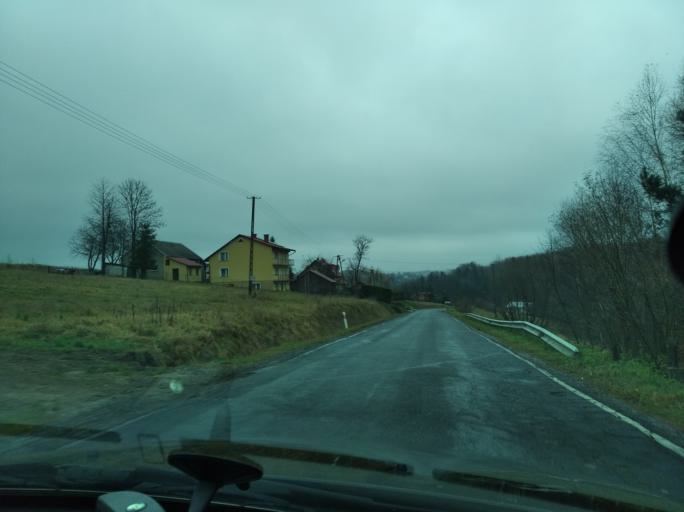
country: PL
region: Subcarpathian Voivodeship
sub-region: Powiat przeworski
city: Jawornik Polski
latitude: 49.8867
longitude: 22.2599
